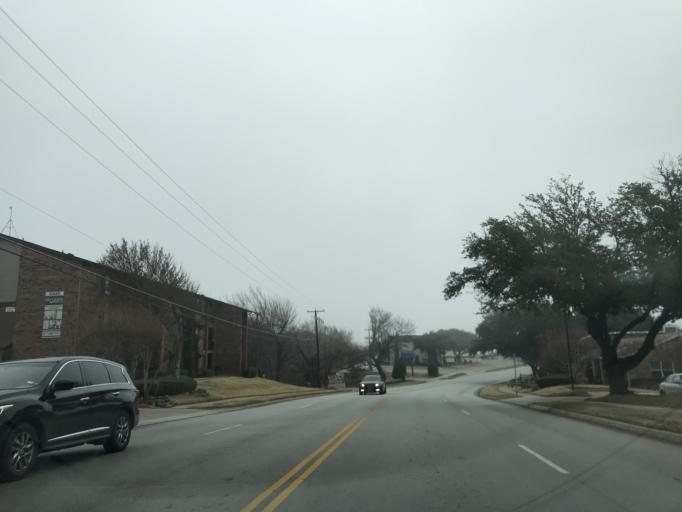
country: US
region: Texas
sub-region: Tarrant County
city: Arlington
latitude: 32.7743
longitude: -97.0657
